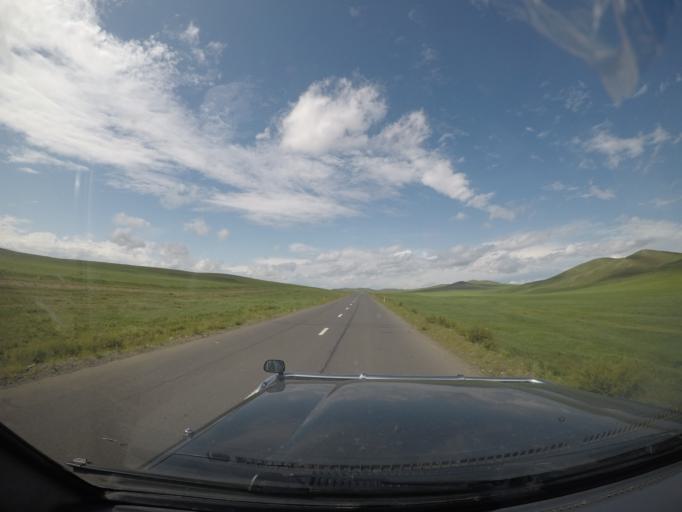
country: MN
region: Hentiy
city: Bayanbulag
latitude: 47.4447
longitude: 109.8301
